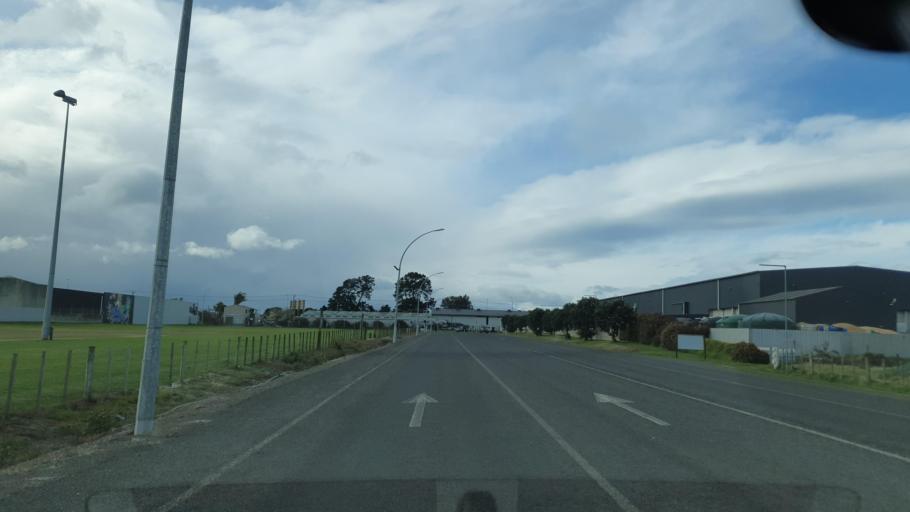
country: NZ
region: Bay of Plenty
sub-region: Tauranga City
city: Tauranga
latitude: -37.6870
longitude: 176.2280
